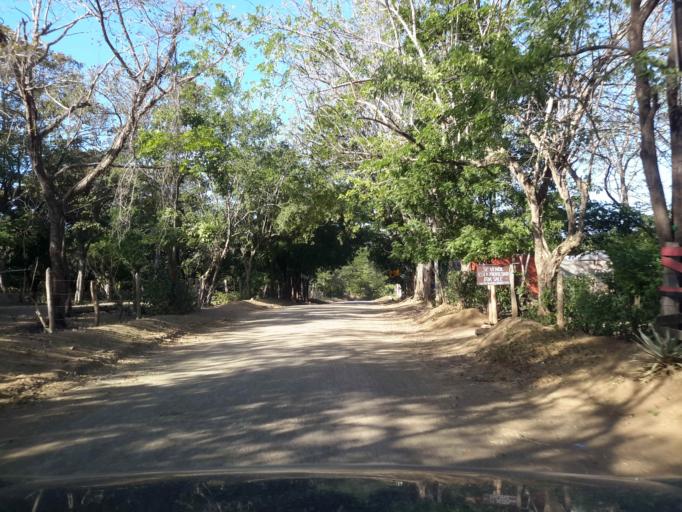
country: NI
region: Rivas
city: San Juan del Sur
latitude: 11.2021
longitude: -85.8041
